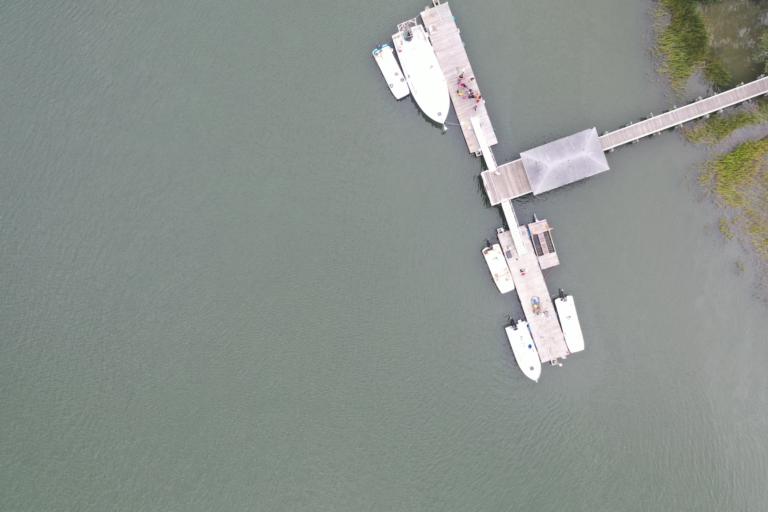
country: US
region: Georgia
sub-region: Chatham County
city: Isle of Hope
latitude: 31.9894
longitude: -81.0242
